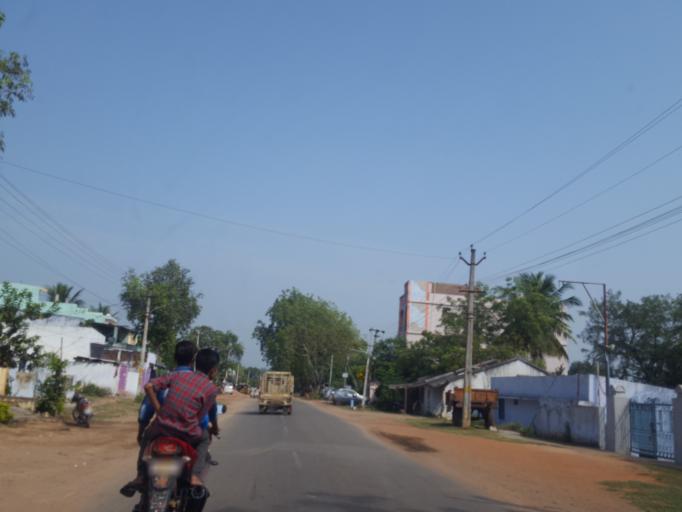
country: IN
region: Telangana
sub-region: Khammam
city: Yellandu
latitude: 17.5986
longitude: 80.3174
